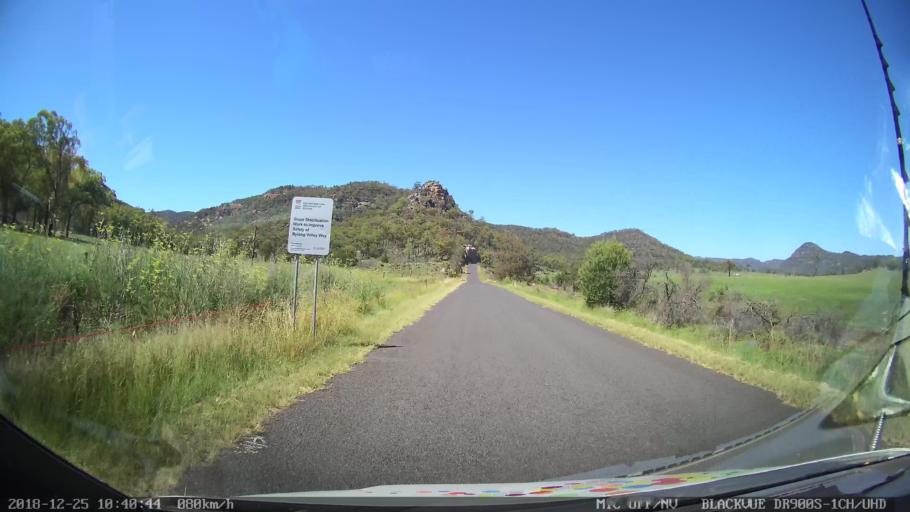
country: AU
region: New South Wales
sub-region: Upper Hunter Shire
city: Merriwa
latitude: -32.4106
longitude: 150.3411
